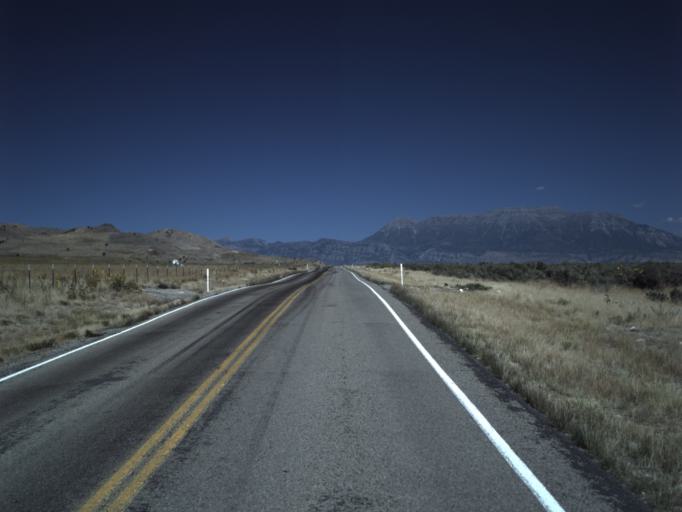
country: US
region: Utah
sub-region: Utah County
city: Saratoga Springs
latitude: 40.2025
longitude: -111.8983
